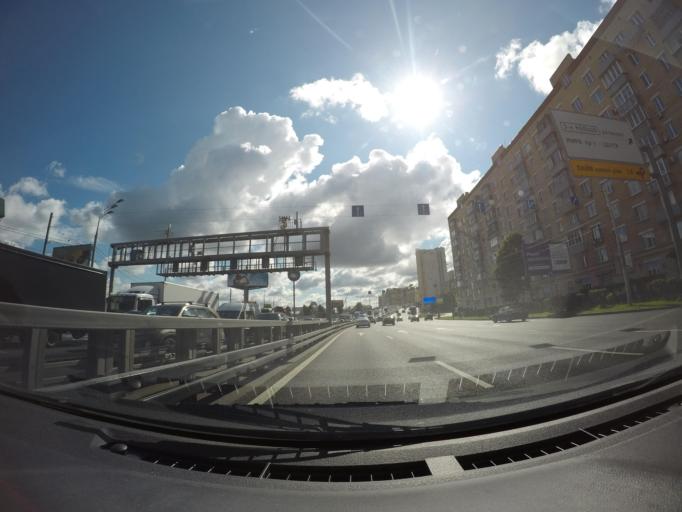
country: RU
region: Moscow
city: Mar'ina Roshcha
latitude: 55.7929
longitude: 37.6274
